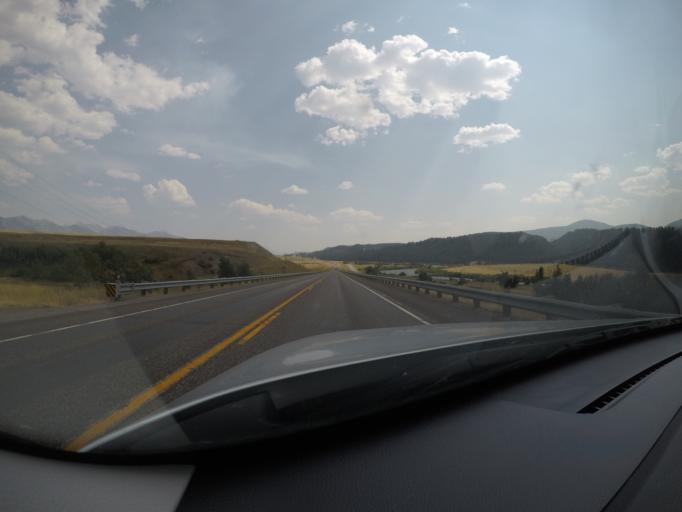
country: US
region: Montana
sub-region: Gallatin County
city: Big Sky
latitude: 44.9793
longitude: -111.6467
